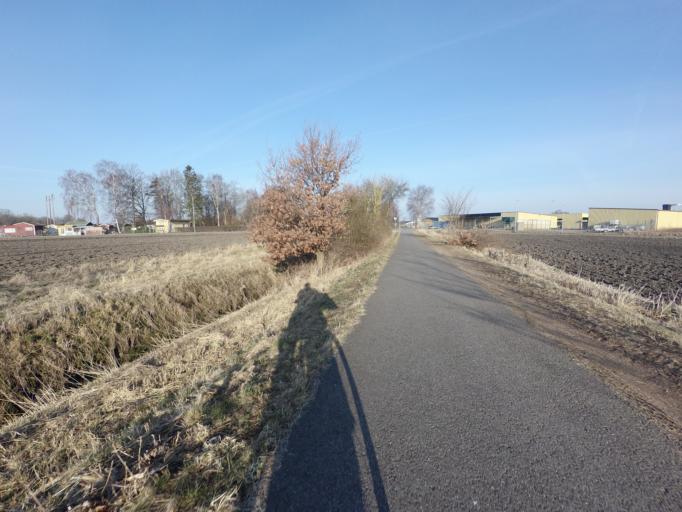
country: SE
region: Skane
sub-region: Hoganas Kommun
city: Hoganas
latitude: 56.1995
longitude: 12.5877
